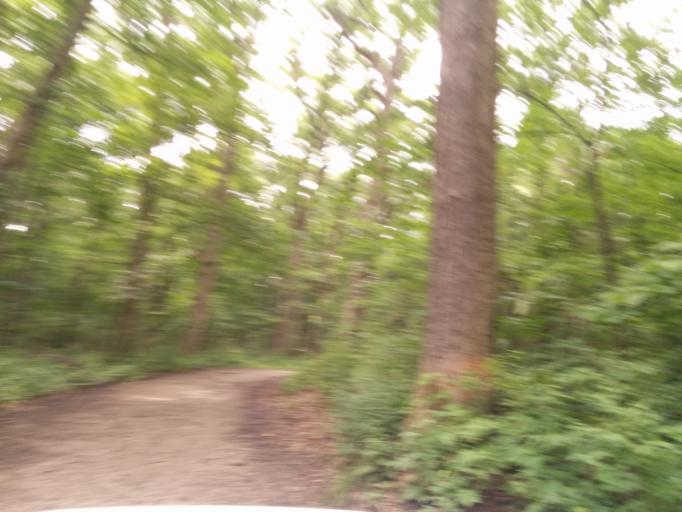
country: US
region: Illinois
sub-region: Cook County
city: Palos Park
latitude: 41.6761
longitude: -87.8399
